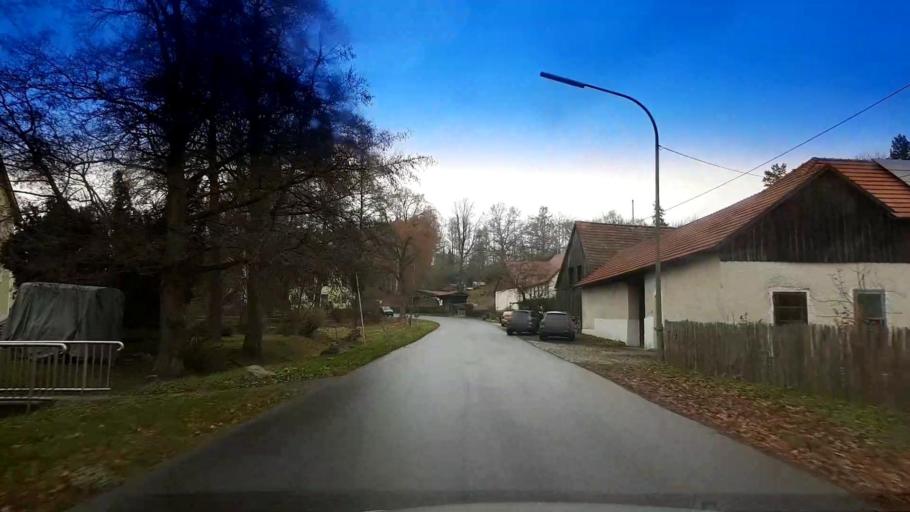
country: DE
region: Bavaria
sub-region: Upper Palatinate
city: Waldsassen
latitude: 50.0257
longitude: 12.3297
